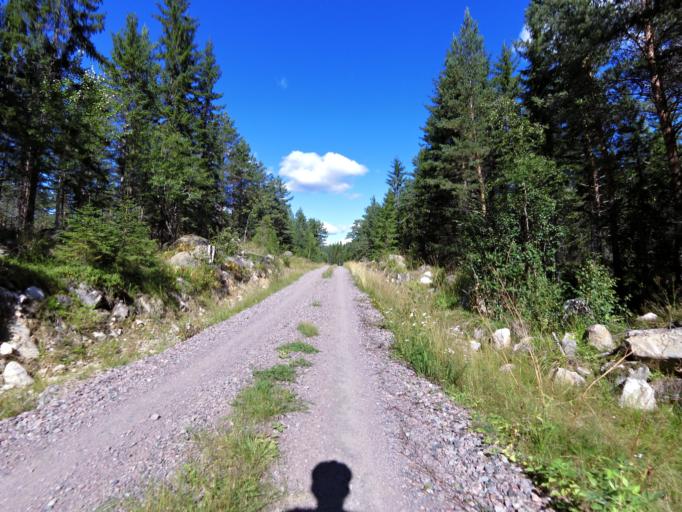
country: SE
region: Gaevleborg
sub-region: Gavle Kommun
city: Valbo
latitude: 60.7346
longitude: 16.9871
